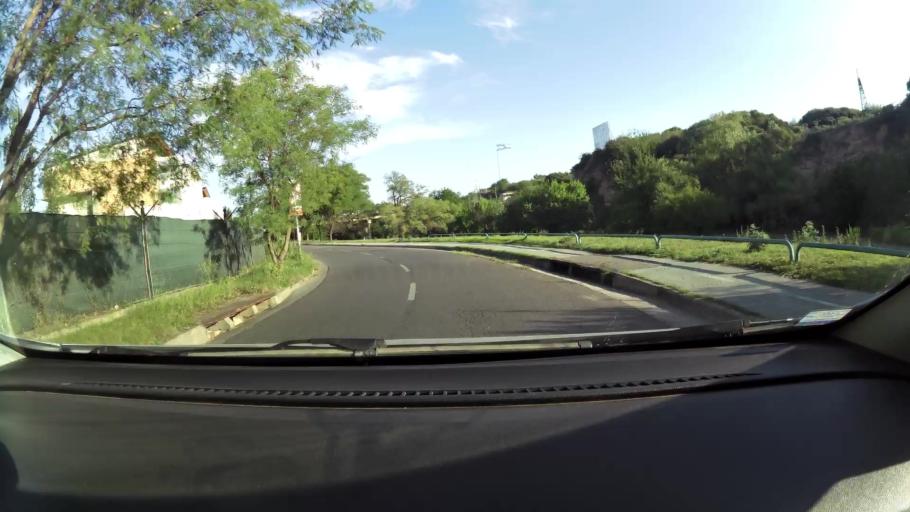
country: AR
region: Cordoba
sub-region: Departamento de Capital
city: Cordoba
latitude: -31.3828
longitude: -64.2485
